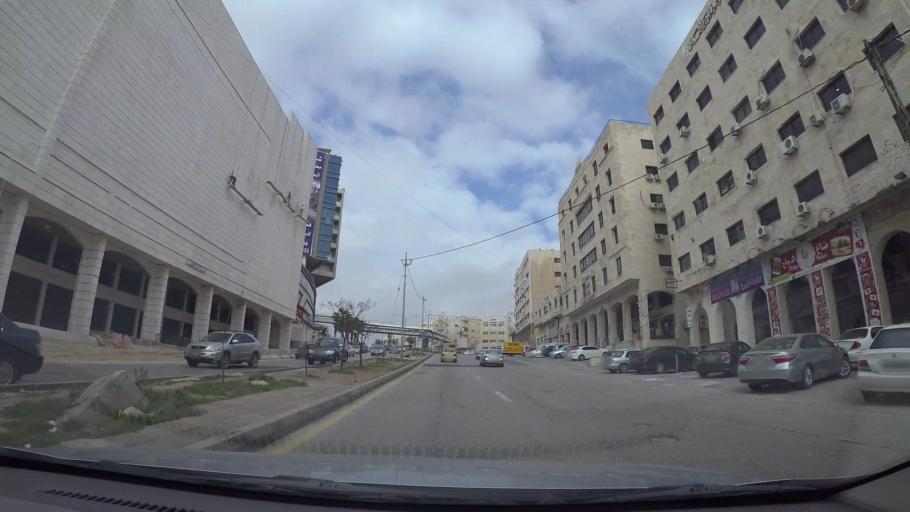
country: JO
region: Amman
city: Al Jubayhah
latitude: 31.9929
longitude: 35.8648
